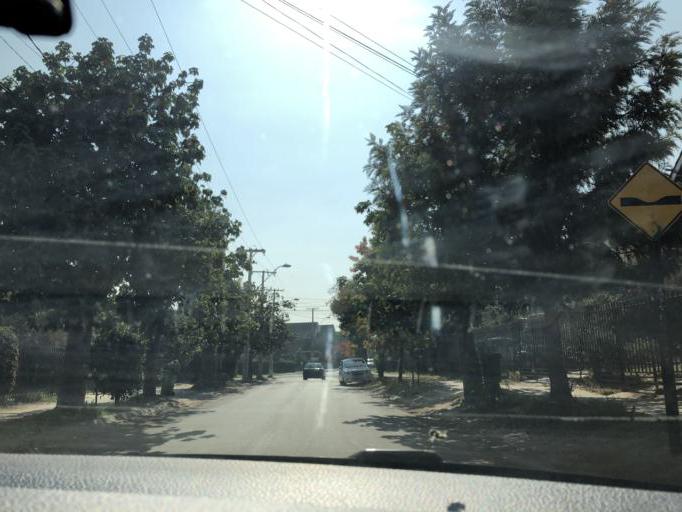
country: CL
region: Santiago Metropolitan
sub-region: Provincia de Cordillera
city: Puente Alto
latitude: -33.5650
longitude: -70.5474
